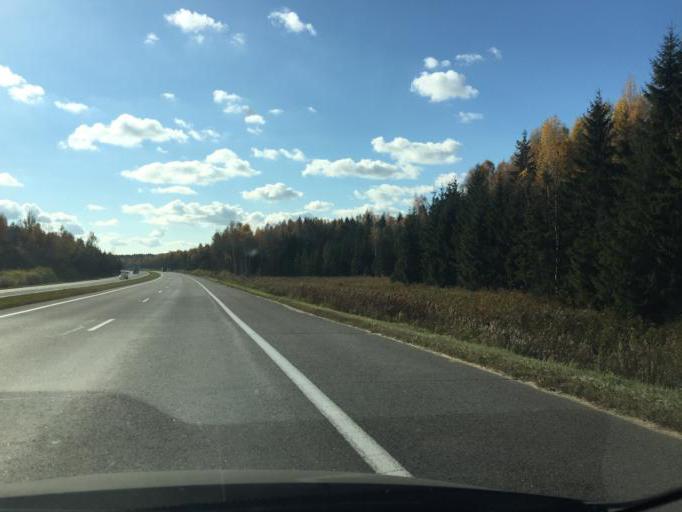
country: BY
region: Minsk
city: Slabada
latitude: 53.9416
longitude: 27.9671
